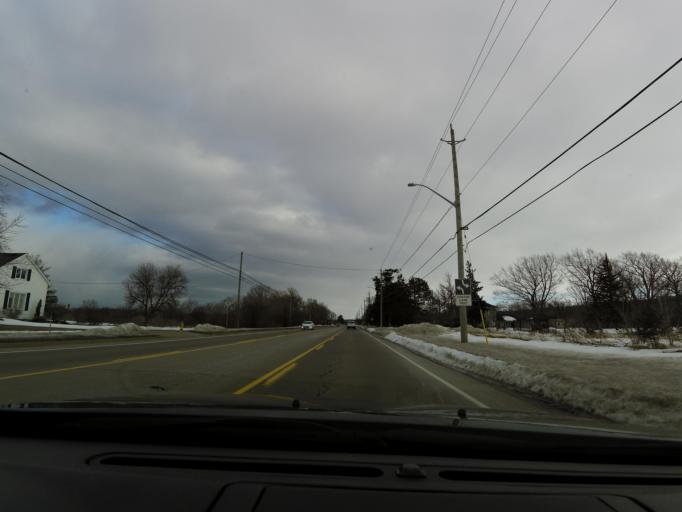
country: CA
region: Ontario
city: Hamilton
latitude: 43.2057
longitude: -79.6227
